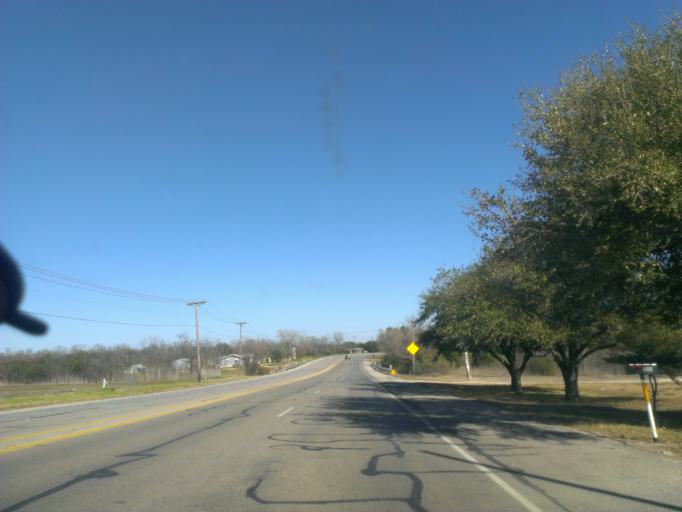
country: US
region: Texas
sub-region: Williamson County
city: Taylor
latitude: 30.5734
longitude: -97.3960
